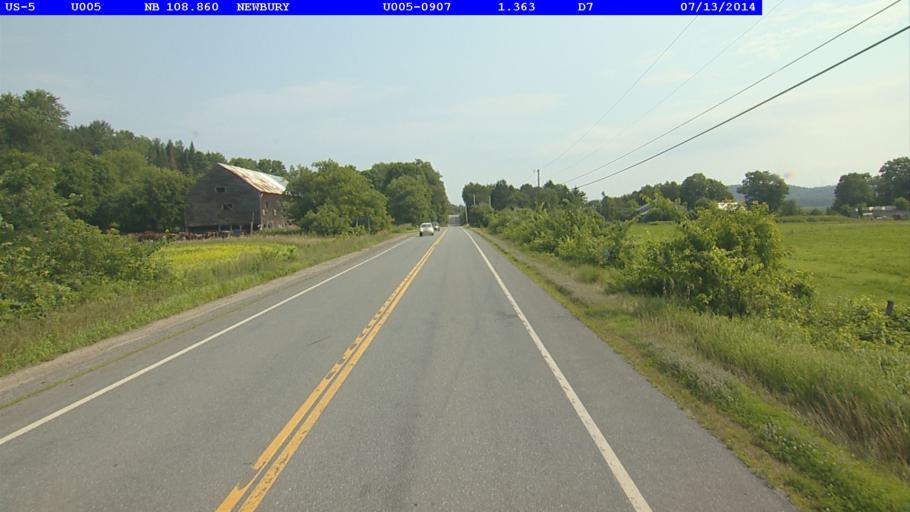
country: US
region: New Hampshire
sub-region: Grafton County
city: Haverhill
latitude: 44.0491
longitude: -72.0761
